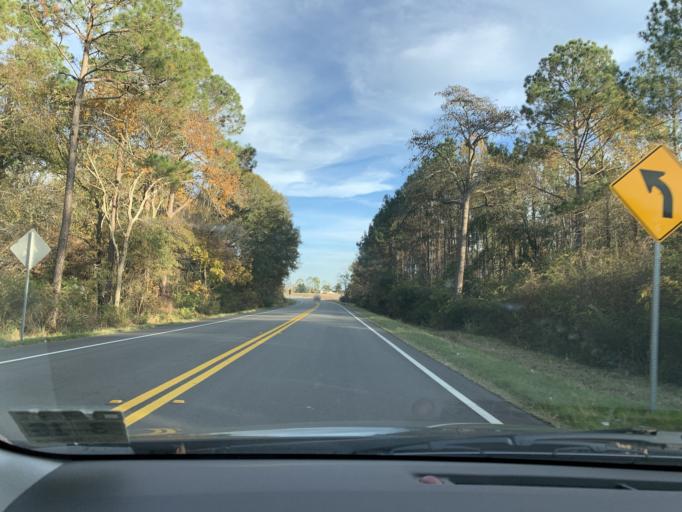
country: US
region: Georgia
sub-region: Irwin County
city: Ocilla
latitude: 31.5934
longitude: -83.2382
